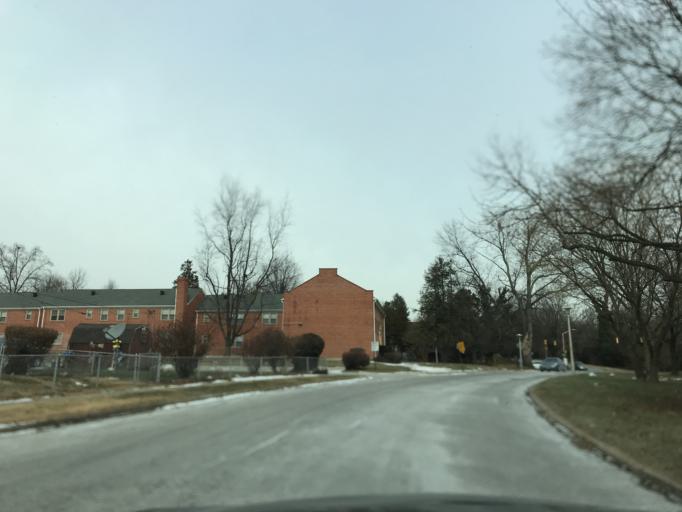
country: US
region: Maryland
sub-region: Baltimore County
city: Towson
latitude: 39.3587
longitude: -76.5991
